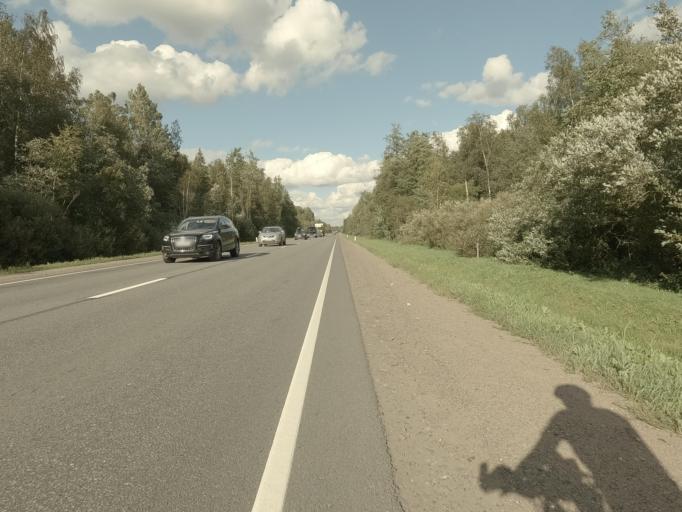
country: RU
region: Leningrad
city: Nikol'skoye
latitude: 59.6552
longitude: 30.8609
